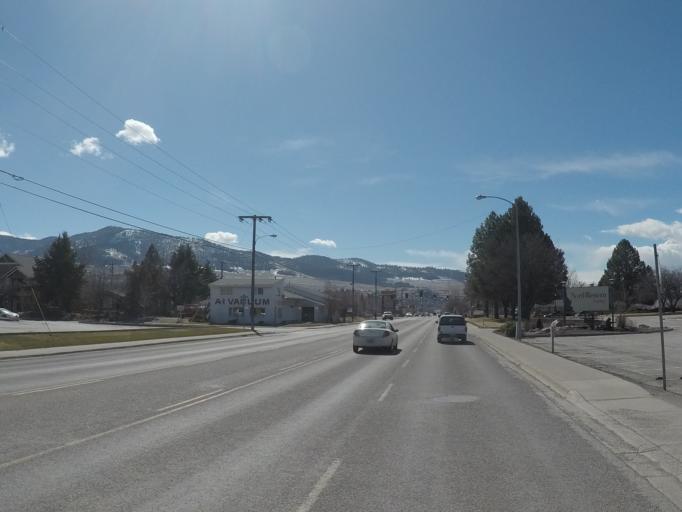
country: US
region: Montana
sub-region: Missoula County
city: Missoula
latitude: 46.8539
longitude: -114.0184
